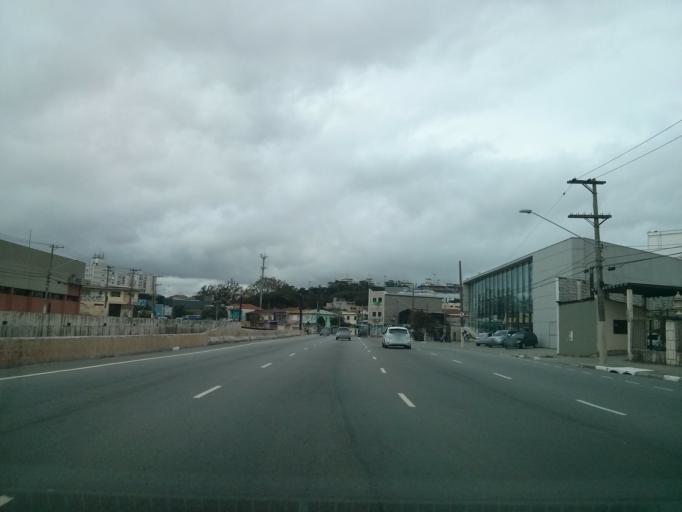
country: BR
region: Sao Paulo
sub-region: Sao Paulo
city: Sao Paulo
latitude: -23.5837
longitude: -46.6167
